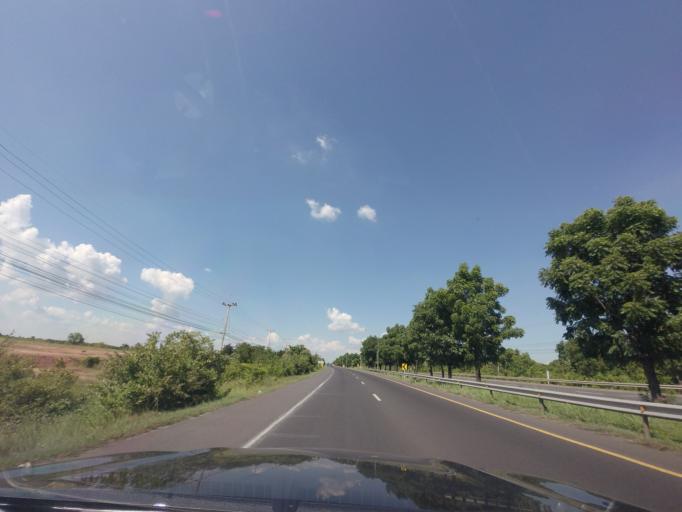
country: TH
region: Nakhon Ratchasima
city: Non Sung
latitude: 15.1926
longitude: 102.3480
